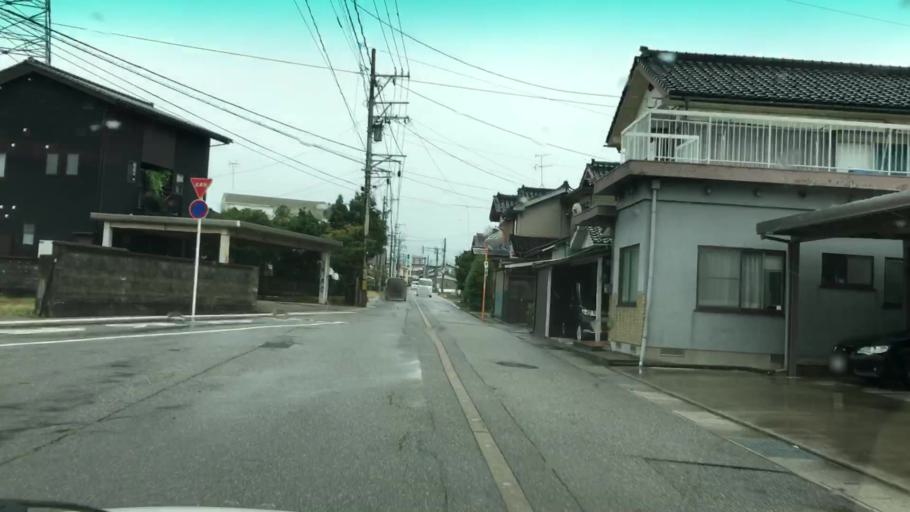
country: JP
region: Toyama
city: Kamiichi
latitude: 36.6522
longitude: 137.3192
